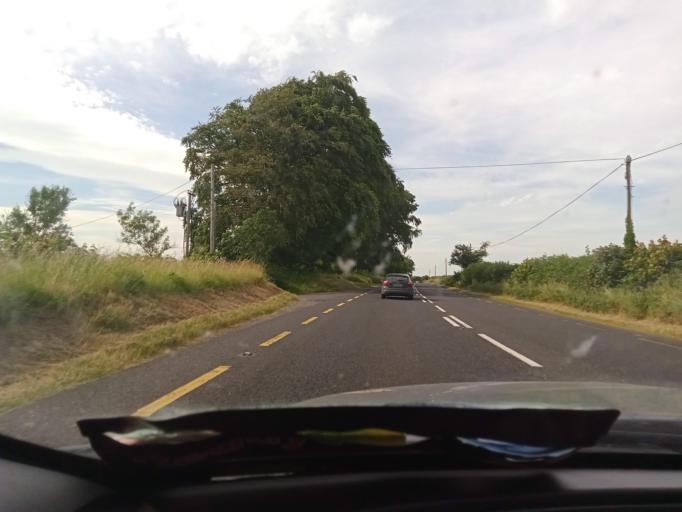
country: IE
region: Leinster
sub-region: Uibh Fhaili
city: Tullamore
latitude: 53.2022
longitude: -7.4327
